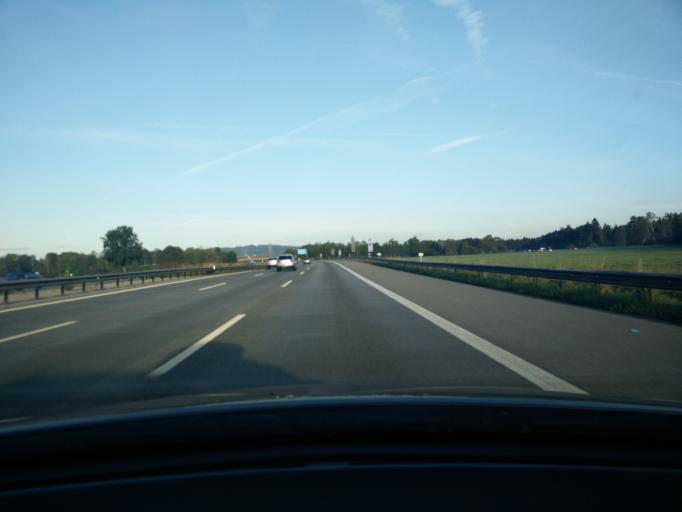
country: DE
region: Bavaria
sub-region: Upper Bavaria
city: Bad Aibling
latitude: 47.8196
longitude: 12.0216
